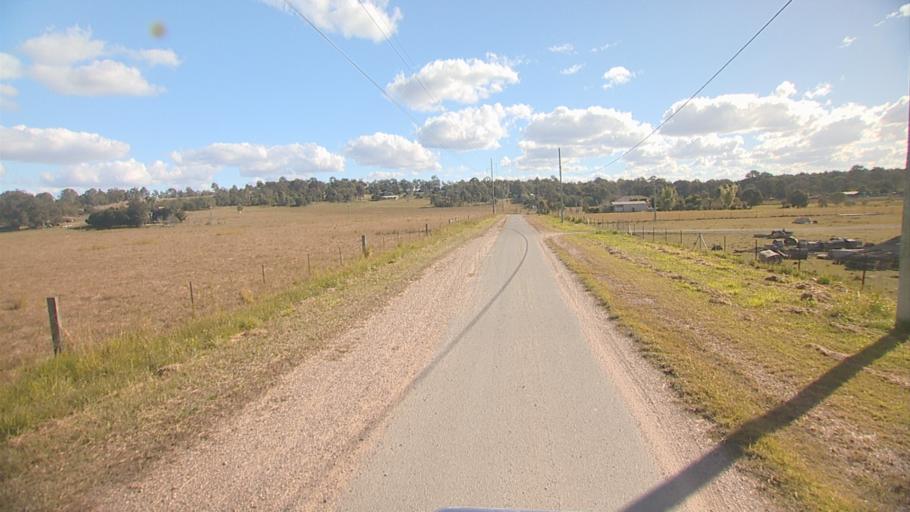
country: AU
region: Queensland
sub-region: Logan
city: Logan Reserve
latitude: -27.7250
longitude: 153.1131
